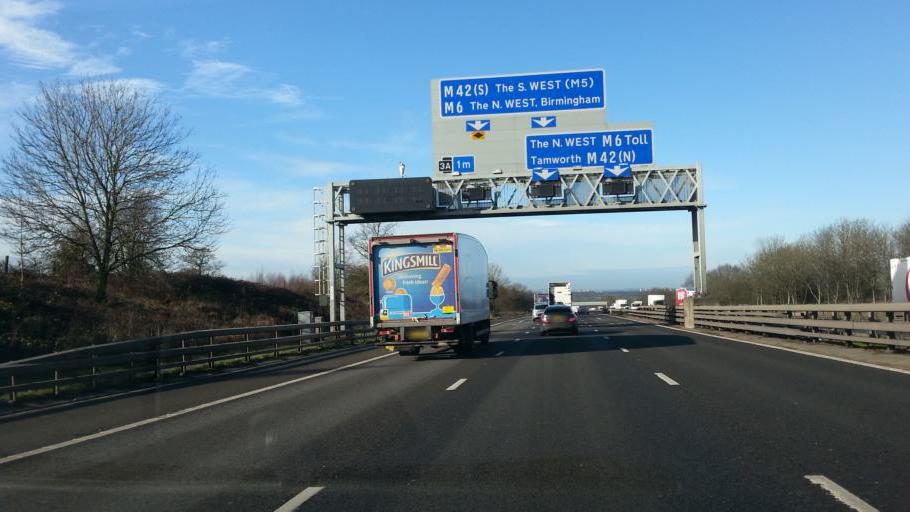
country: GB
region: England
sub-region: Solihull
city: Meriden
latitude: 52.4695
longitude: -1.6447
